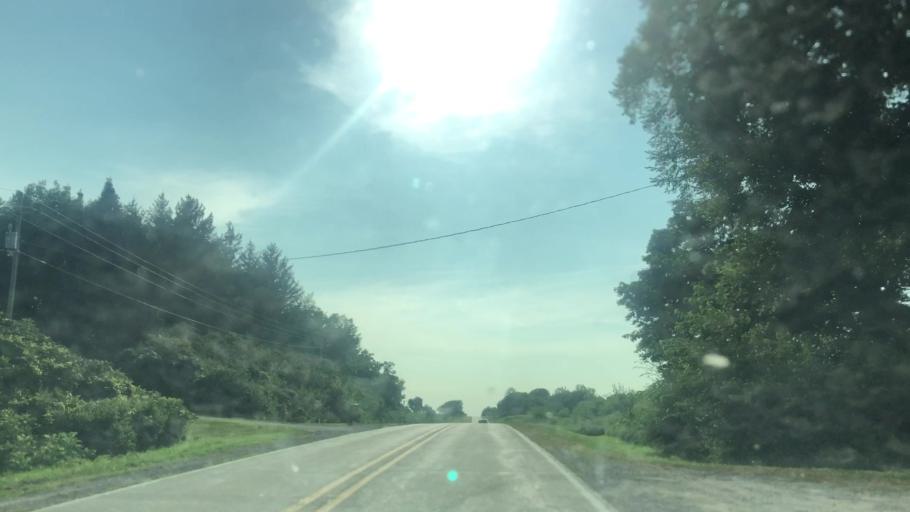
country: US
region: Iowa
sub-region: Marshall County
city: Marshalltown
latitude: 42.0490
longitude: -92.9761
